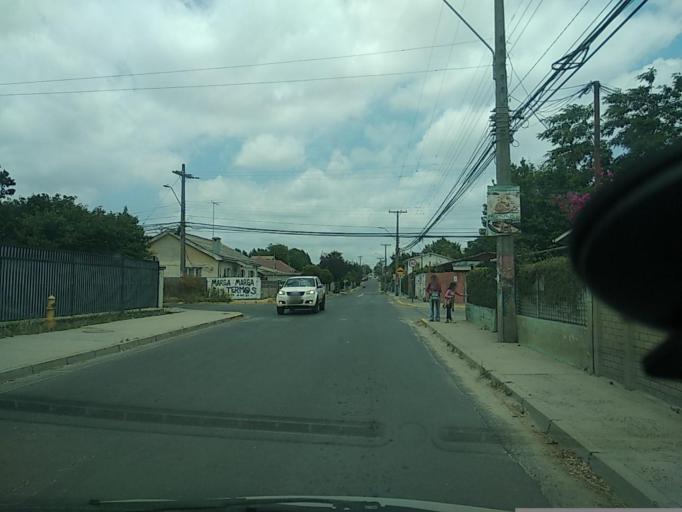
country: CL
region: Valparaiso
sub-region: Provincia de Marga Marga
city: Villa Alemana
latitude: -33.0402
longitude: -71.4076
